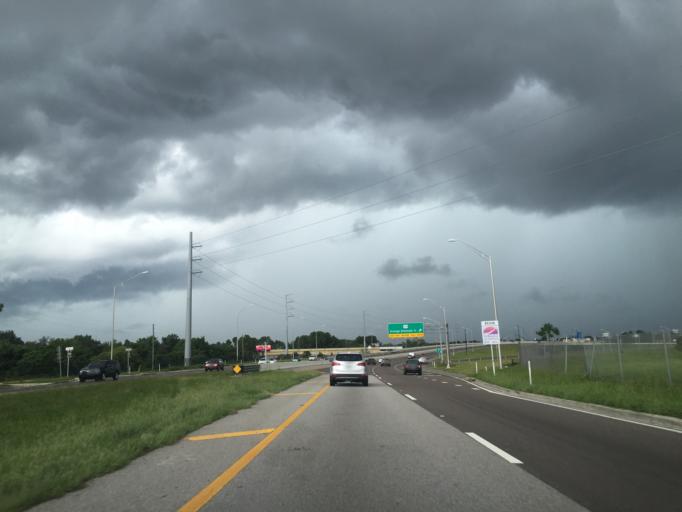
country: US
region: Florida
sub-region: Orange County
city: Lockhart
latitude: 28.6368
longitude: -81.4475
